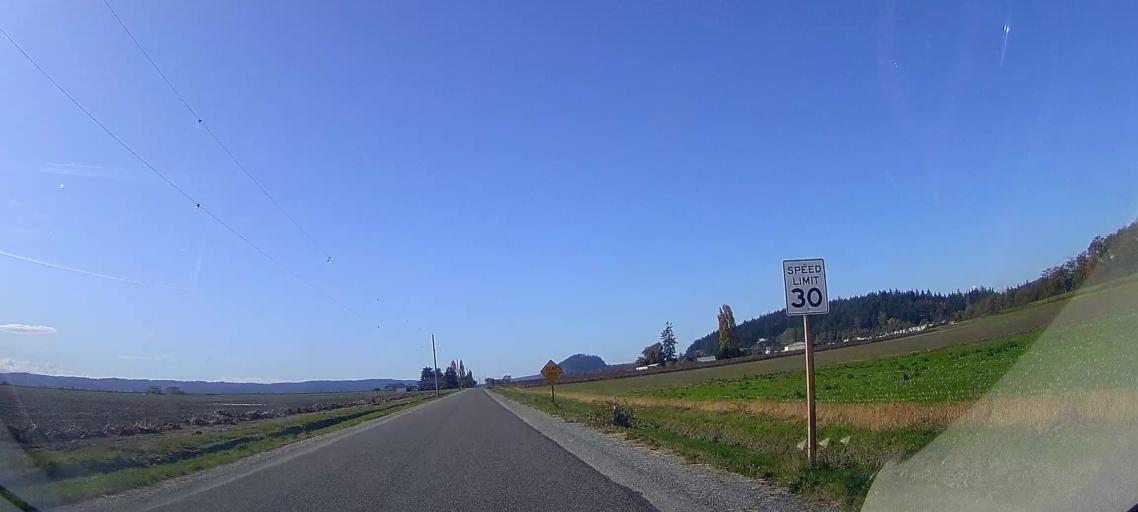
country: US
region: Washington
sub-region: Skagit County
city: Mount Vernon
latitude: 48.3556
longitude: -122.4389
